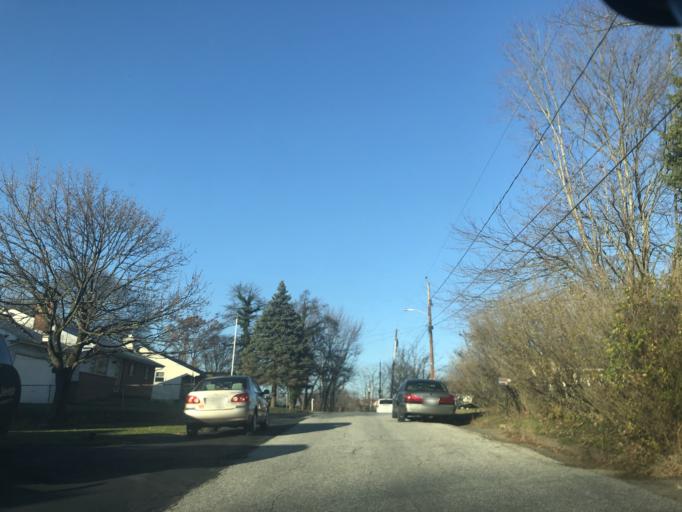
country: US
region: Maryland
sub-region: Baltimore County
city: Catonsville
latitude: 39.2828
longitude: -76.7372
